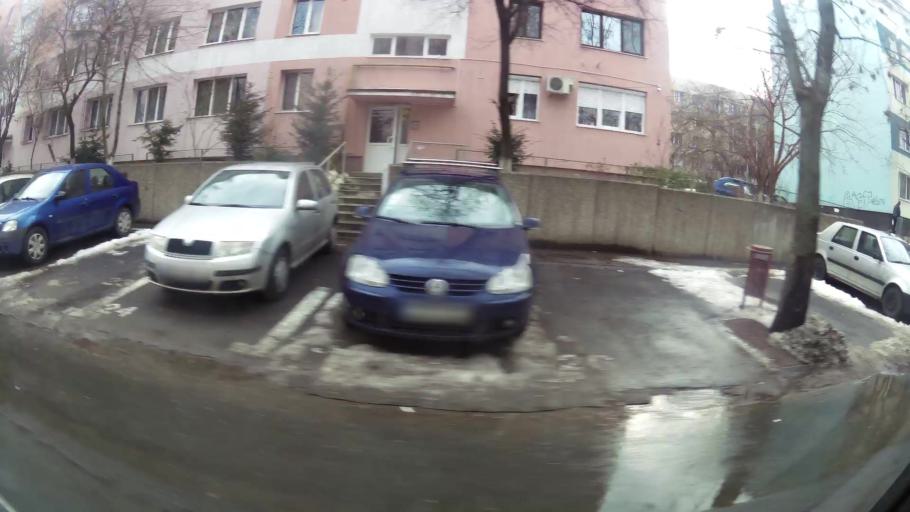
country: RO
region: Ilfov
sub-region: Comuna Popesti-Leordeni
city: Popesti-Leordeni
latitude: 44.4077
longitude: 26.1757
